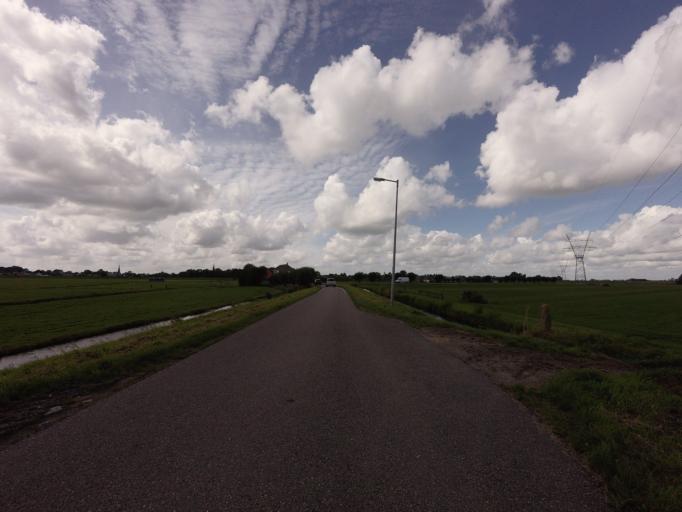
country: NL
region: North Holland
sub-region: Gemeente Purmerend
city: Purmerend
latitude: 52.4643
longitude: 4.9622
